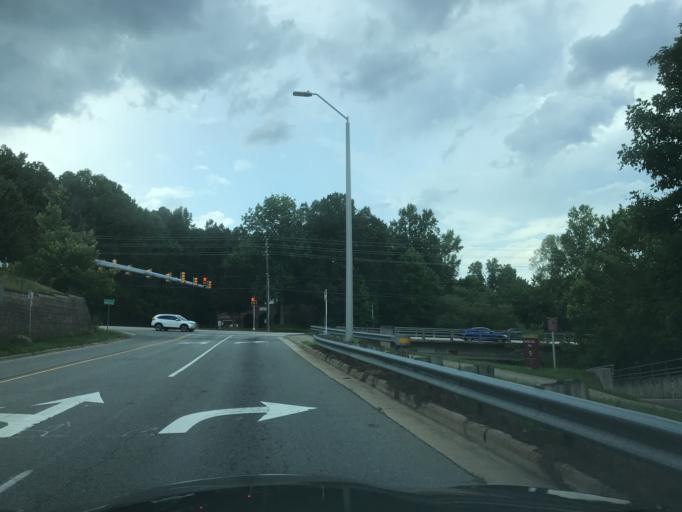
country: US
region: North Carolina
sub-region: Wake County
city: West Raleigh
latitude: 35.8408
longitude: -78.6838
